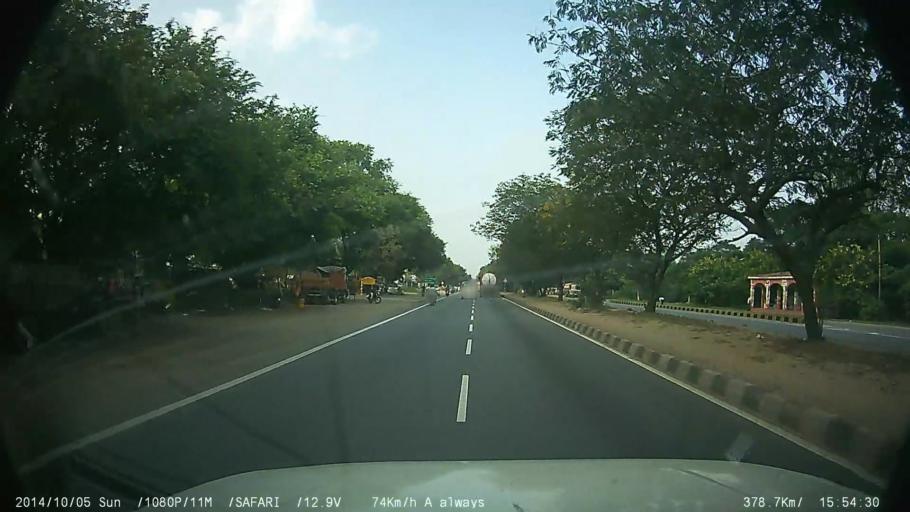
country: IN
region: Tamil Nadu
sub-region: Kancheepuram
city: Singapperumalkovil
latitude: 12.7935
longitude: 80.0191
